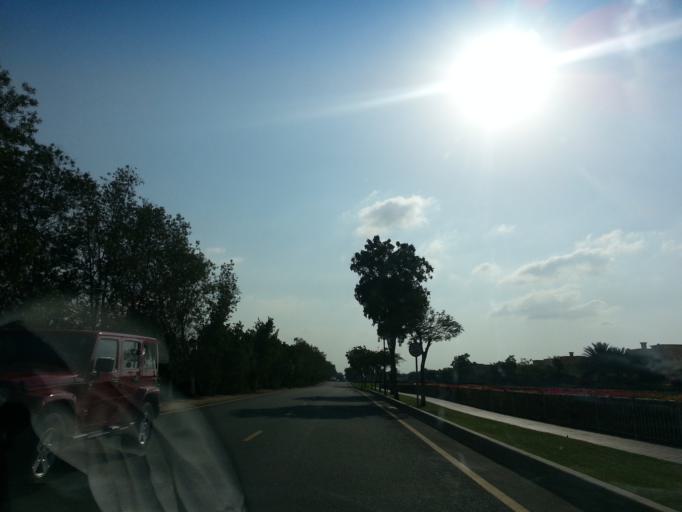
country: AE
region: Dubai
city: Dubai
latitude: 25.0574
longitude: 55.1878
